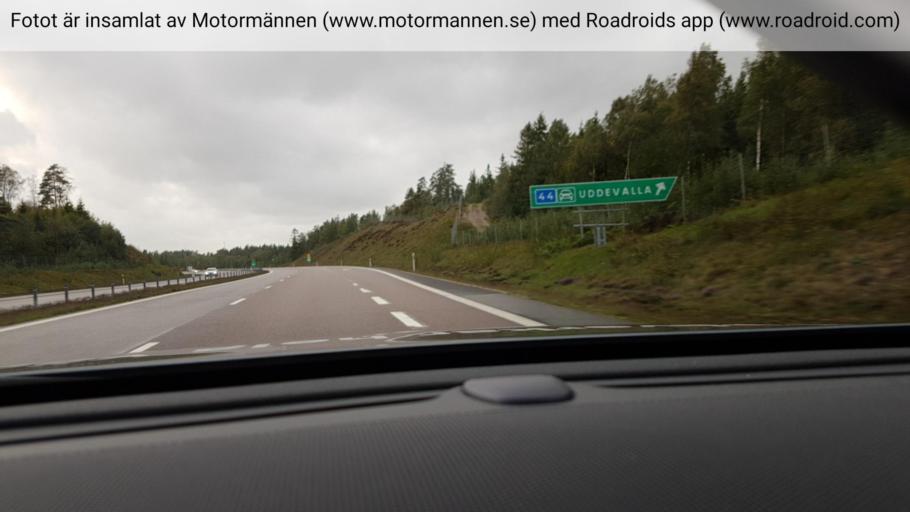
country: SE
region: Vaestra Goetaland
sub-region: Uddevalla Kommun
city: Uddevalla
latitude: 58.3353
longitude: 11.9976
